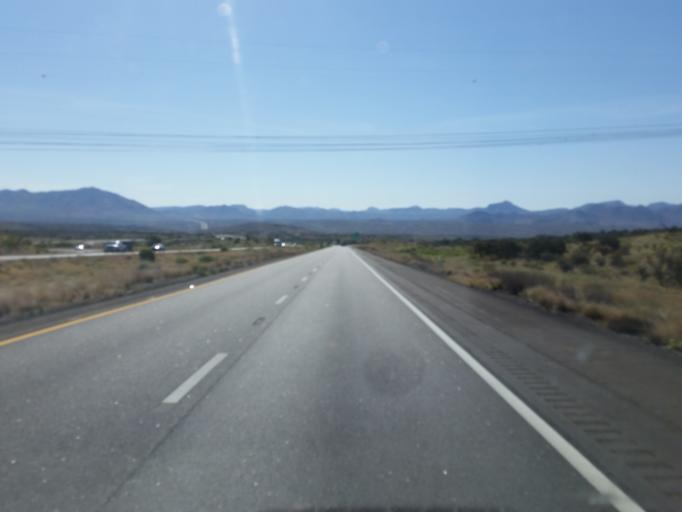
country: US
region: Arizona
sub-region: Mohave County
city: New Kingman-Butler
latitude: 35.1602
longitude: -113.7058
